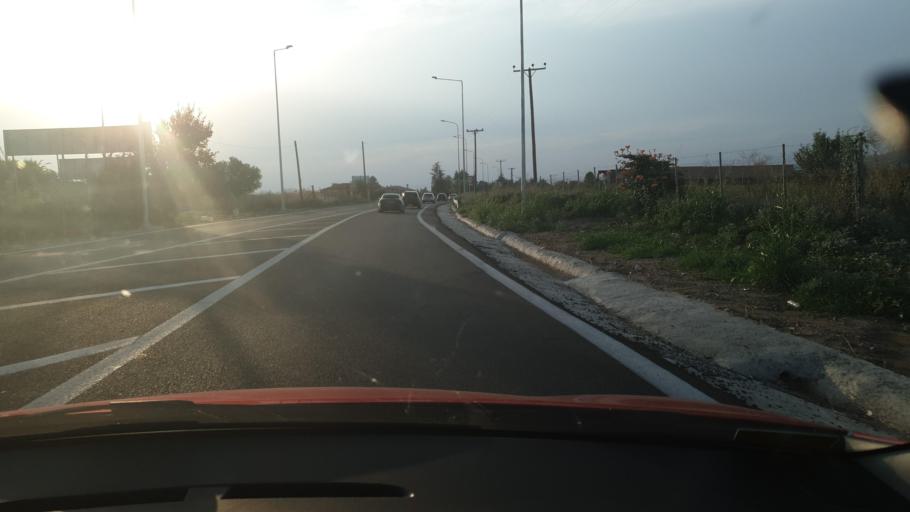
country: GR
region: Central Macedonia
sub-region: Nomos Thessalonikis
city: Souroti
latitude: 40.5020
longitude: 23.0964
